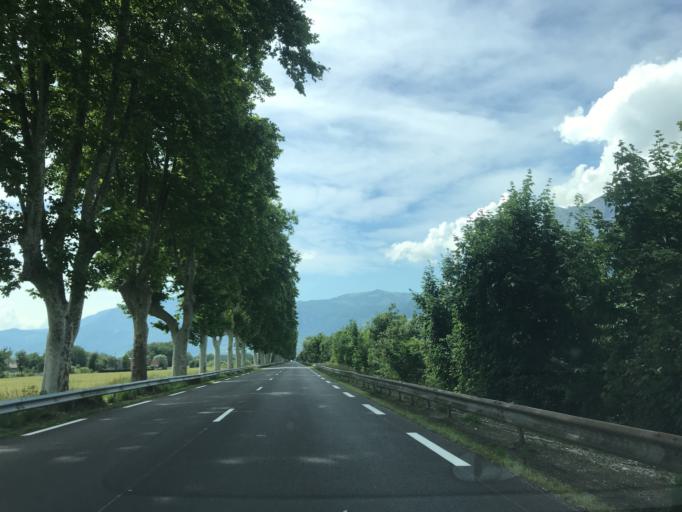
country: FR
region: Rhone-Alpes
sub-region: Departement de la Savoie
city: Aiton
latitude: 45.5556
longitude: 6.2411
